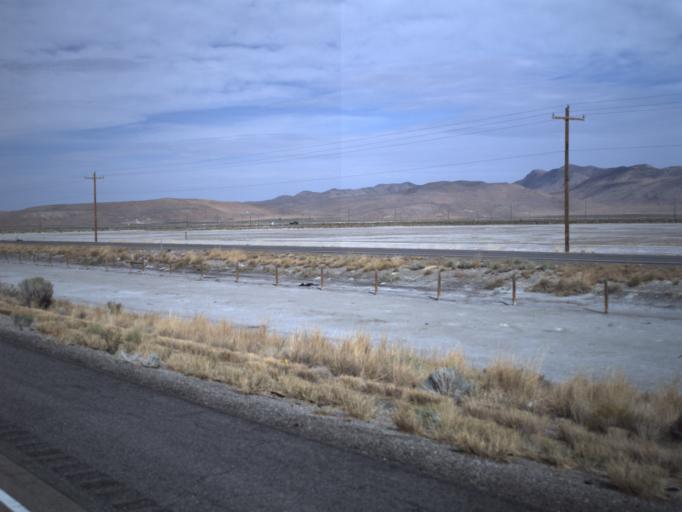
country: US
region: Utah
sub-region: Tooele County
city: Grantsville
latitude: 40.7533
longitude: -112.7246
